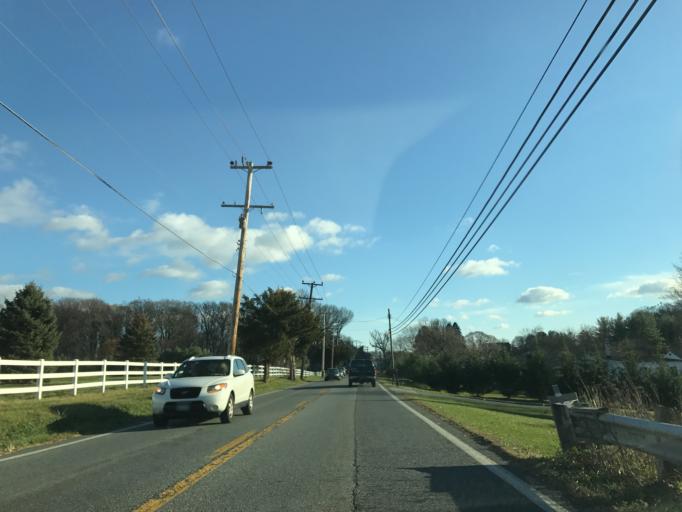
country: US
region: Maryland
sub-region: Harford County
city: Jarrettsville
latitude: 39.6225
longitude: -76.5492
